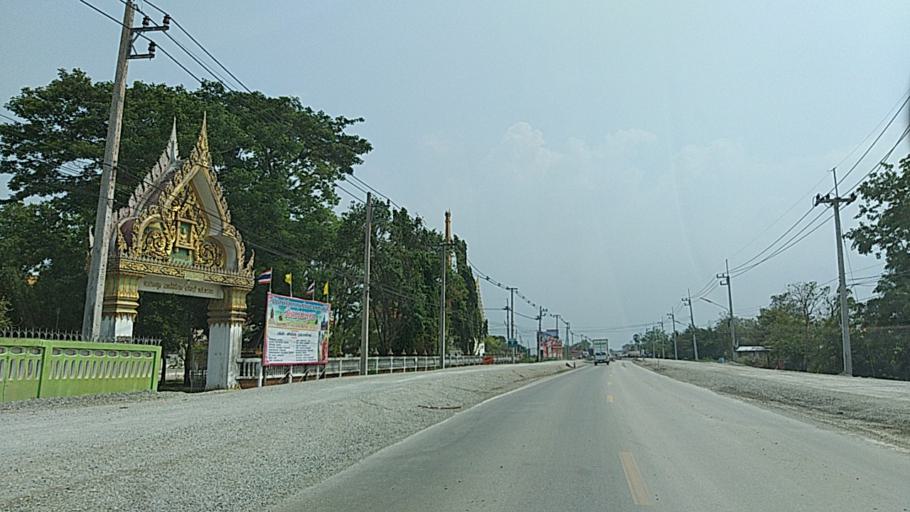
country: TH
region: Chon Buri
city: Phanat Nikhom
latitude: 13.4210
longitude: 101.1866
